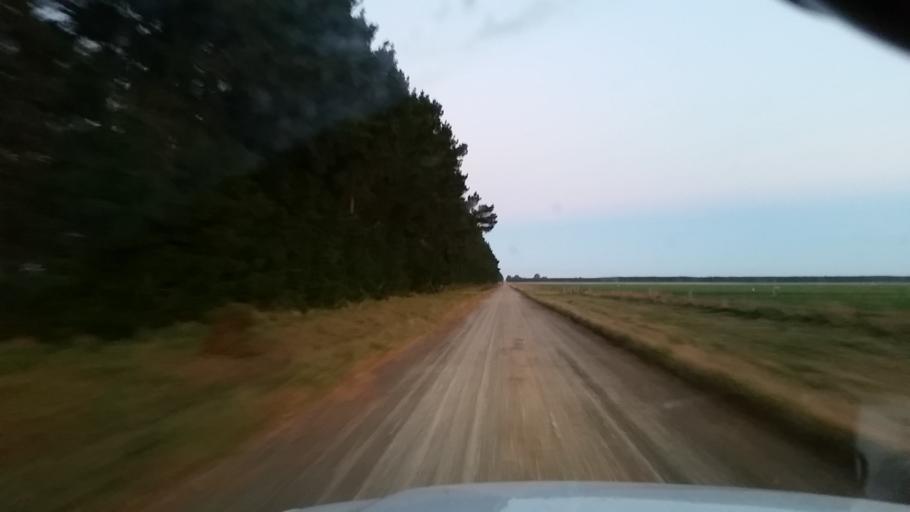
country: NZ
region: Canterbury
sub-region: Ashburton District
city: Tinwald
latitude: -43.9515
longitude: 171.6168
